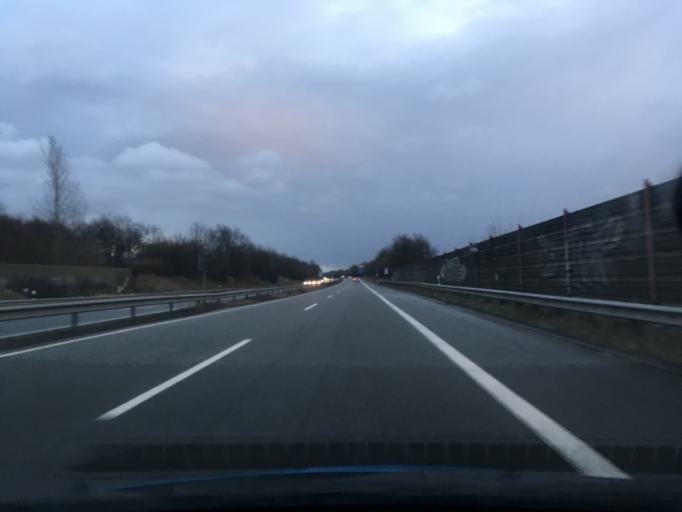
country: DE
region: Lower Saxony
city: Bardowick
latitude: 53.2851
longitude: 10.3848
